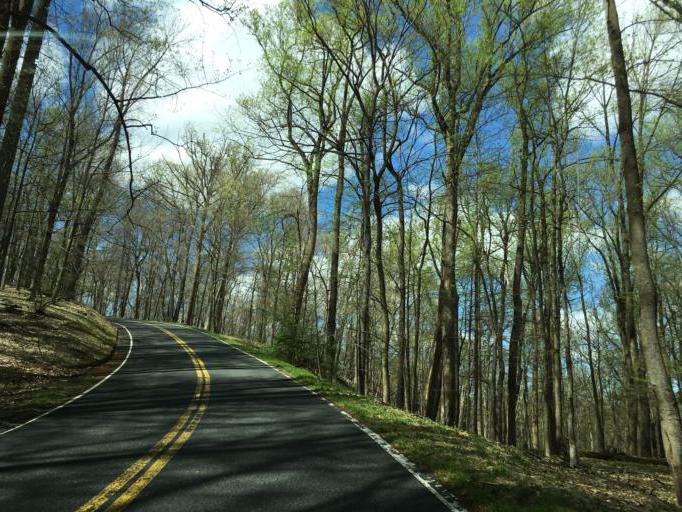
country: US
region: Maryland
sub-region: Frederick County
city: Thurmont
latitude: 39.6476
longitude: -77.4441
